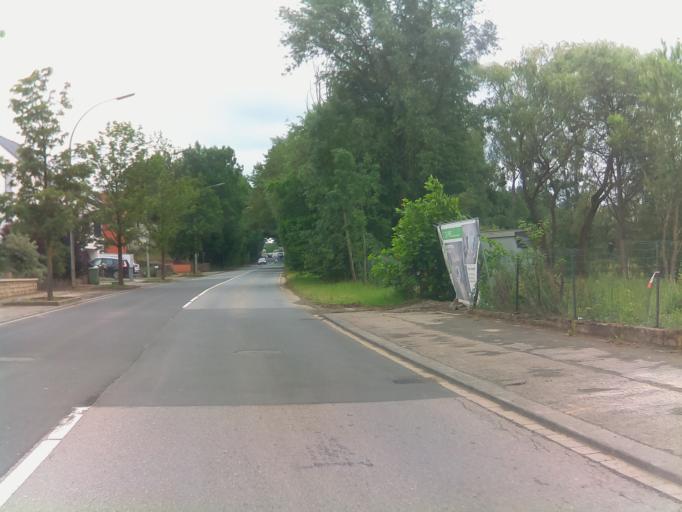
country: LU
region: Luxembourg
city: Pontpierre
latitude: 49.5443
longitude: 6.0174
